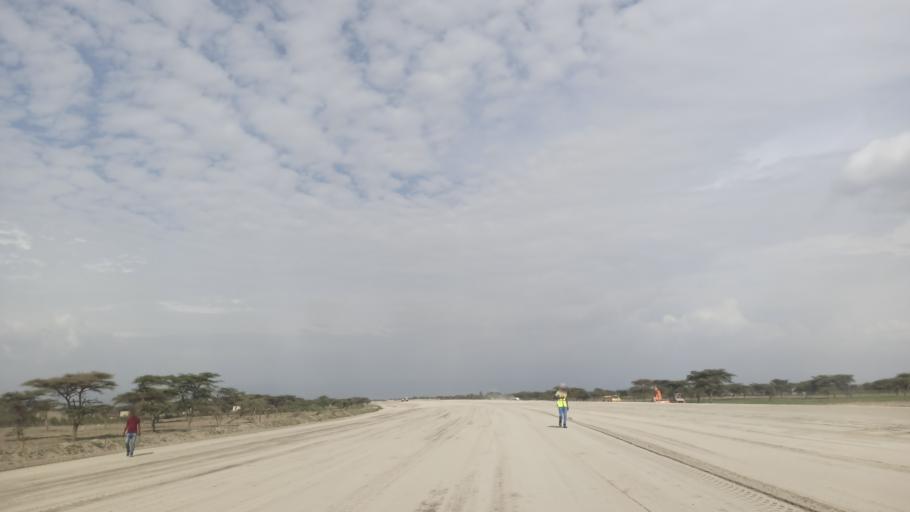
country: ET
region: Oromiya
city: Ziway
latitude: 7.6950
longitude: 38.6480
